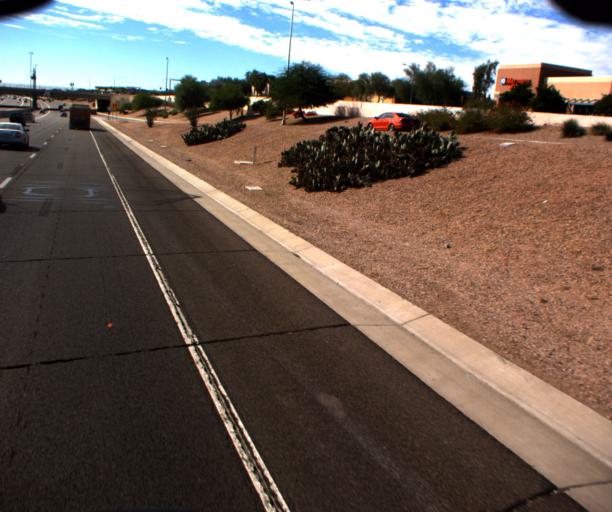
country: US
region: Arizona
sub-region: Maricopa County
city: Paradise Valley
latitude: 33.6211
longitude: -111.8912
